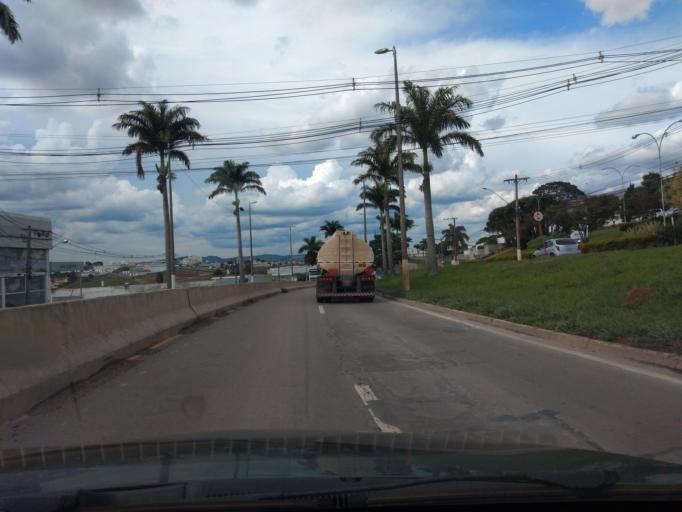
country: BR
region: Minas Gerais
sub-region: Varginha
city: Varginha
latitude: -21.5945
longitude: -45.4395
